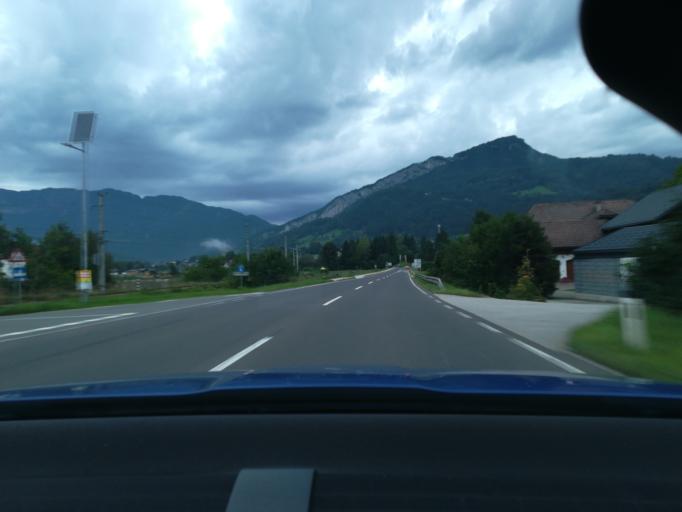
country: AT
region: Upper Austria
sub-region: Politischer Bezirk Gmunden
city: Bad Goisern
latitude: 47.6282
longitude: 13.6292
